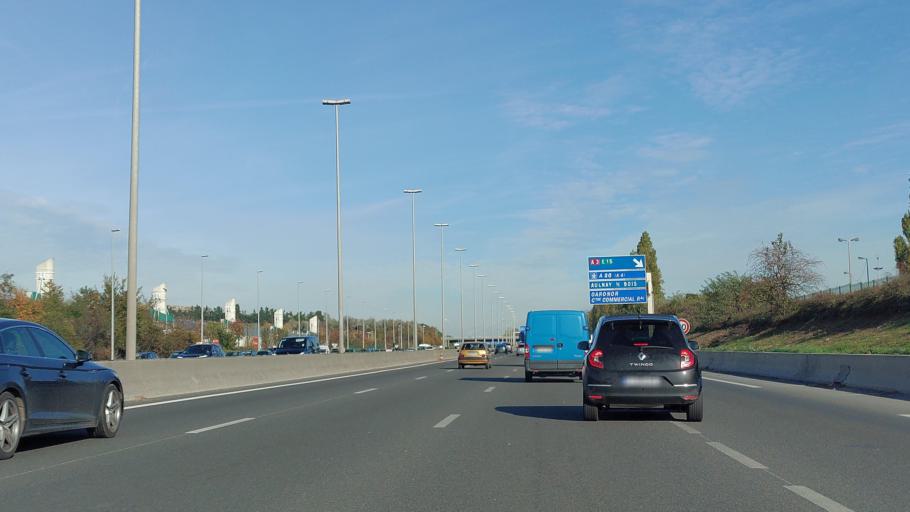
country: FR
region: Ile-de-France
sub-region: Departement de Seine-Saint-Denis
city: Le Blanc-Mesnil
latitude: 48.9551
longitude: 2.4613
